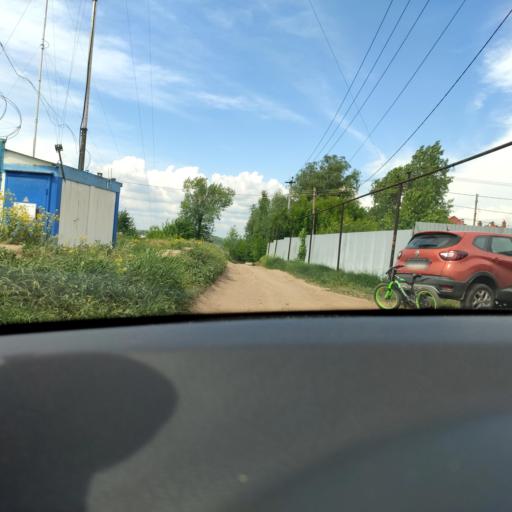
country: RU
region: Samara
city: Novokuybyshevsk
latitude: 53.1500
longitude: 50.0166
